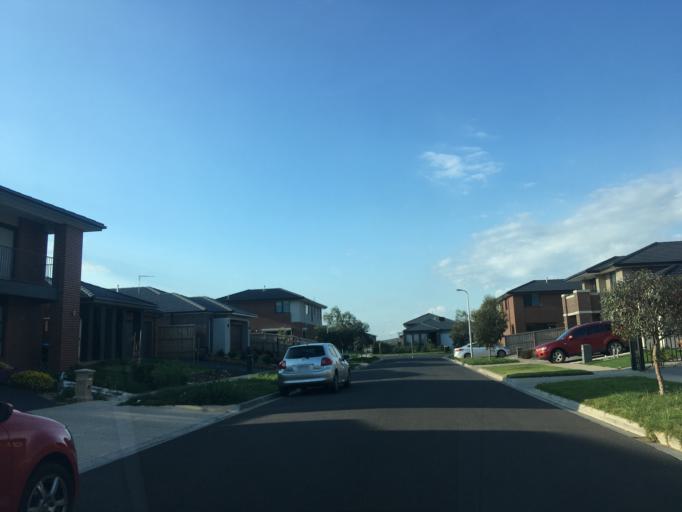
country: AU
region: Victoria
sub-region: Wyndham
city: Hoppers Crossing
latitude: -37.8863
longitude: 144.7173
